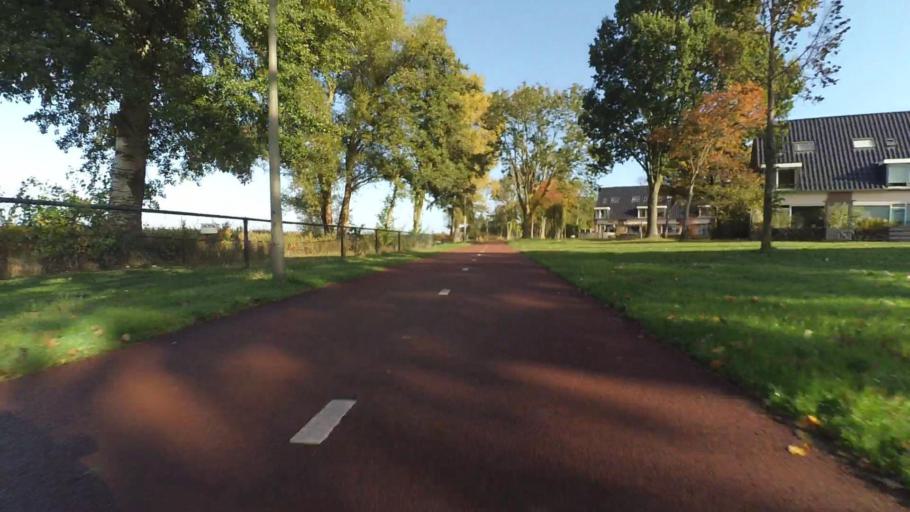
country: NL
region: Gelderland
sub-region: Gemeente Harderwijk
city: Harderwijk
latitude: 52.3439
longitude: 5.6095
